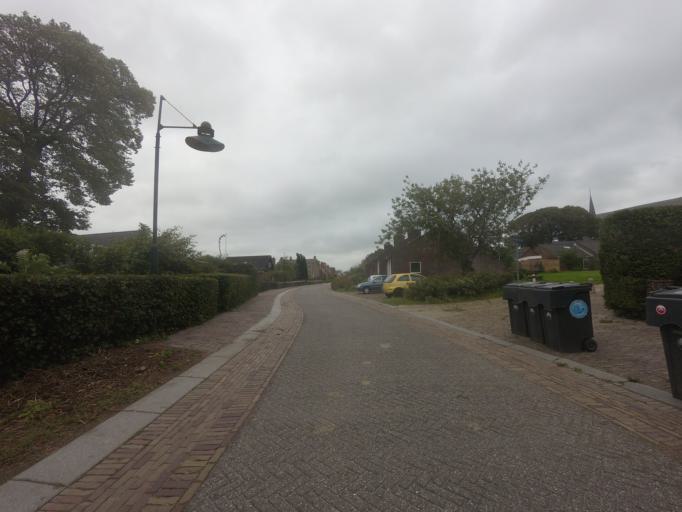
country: NL
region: Friesland
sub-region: Gemeente Ferwerderadiel
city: Hallum
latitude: 53.3082
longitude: 5.7847
